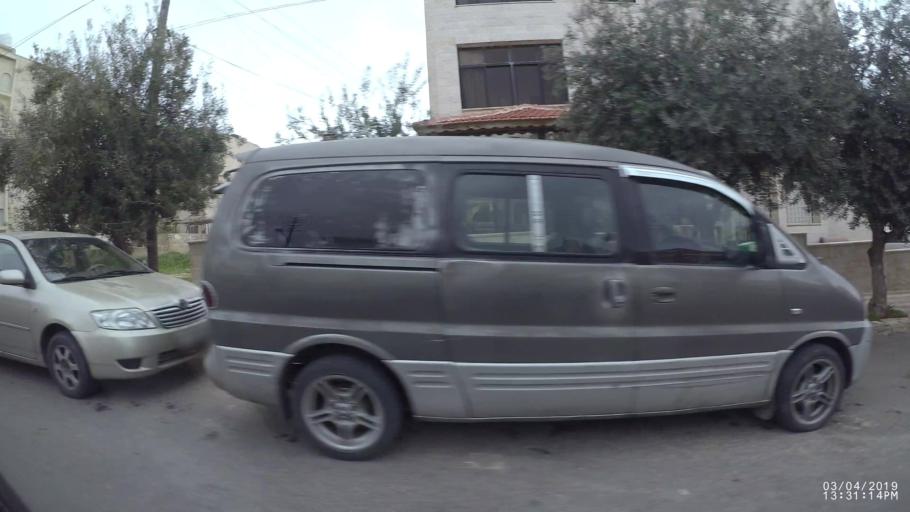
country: JO
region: Amman
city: Wadi as Sir
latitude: 31.9651
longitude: 35.8268
